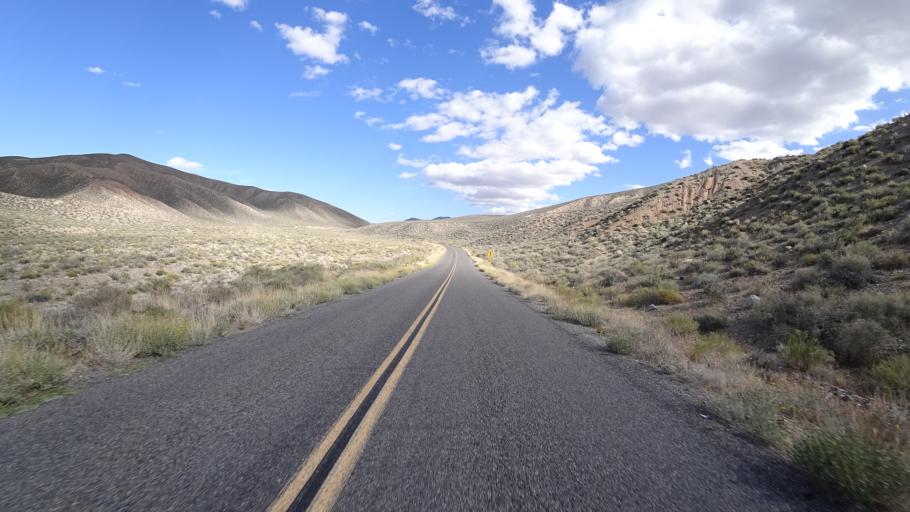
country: US
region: Nevada
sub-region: Nye County
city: Beatty
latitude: 36.4051
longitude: -117.1709
